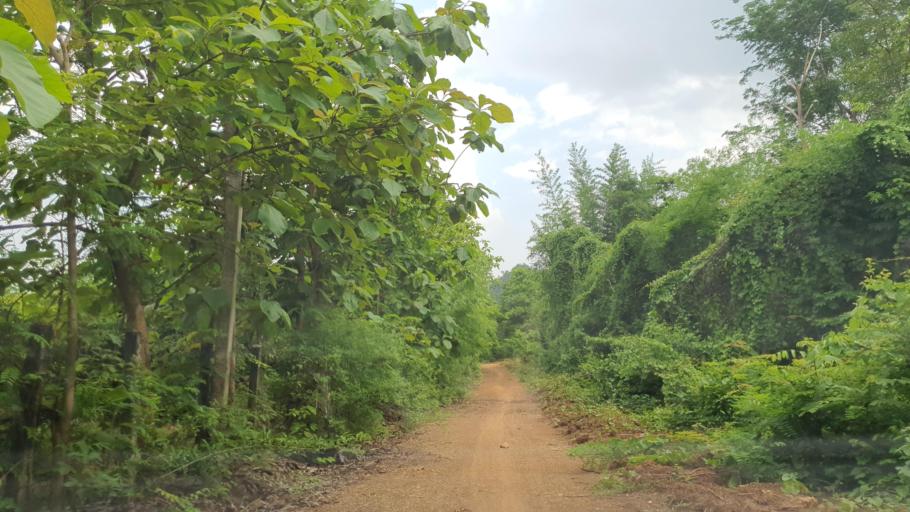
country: TH
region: Sukhothai
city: Thung Saliam
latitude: 17.2430
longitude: 99.5441
